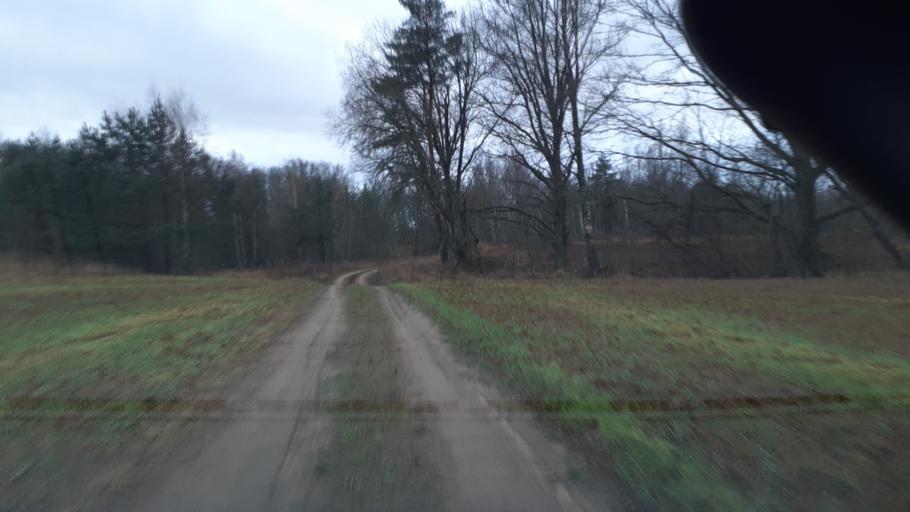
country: LV
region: Kuldigas Rajons
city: Kuldiga
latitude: 56.8805
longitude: 21.7706
